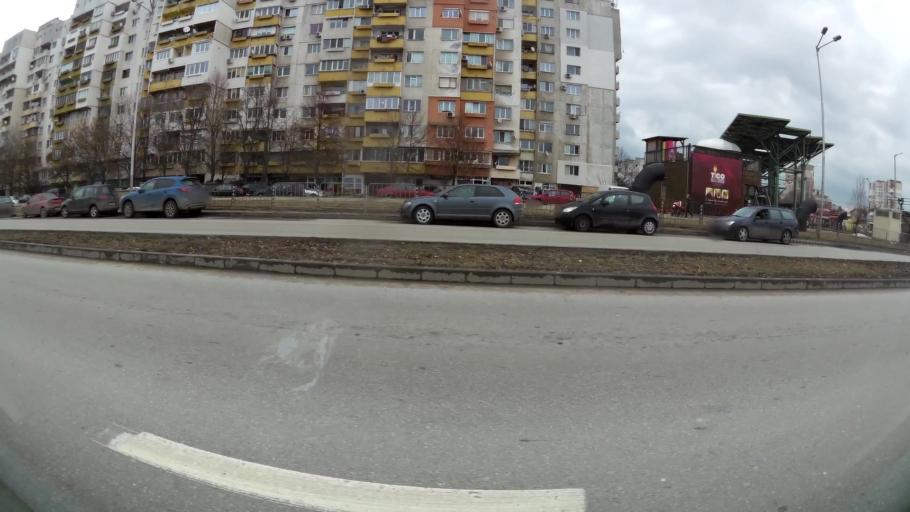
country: BG
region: Sofia-Capital
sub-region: Stolichna Obshtina
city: Sofia
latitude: 42.7358
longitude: 23.2922
